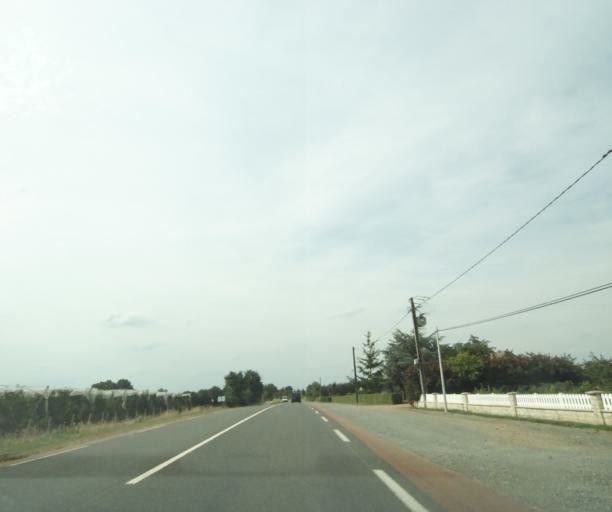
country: FR
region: Pays de la Loire
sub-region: Departement de la Sarthe
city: Luceau
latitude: 47.7366
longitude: 0.3918
